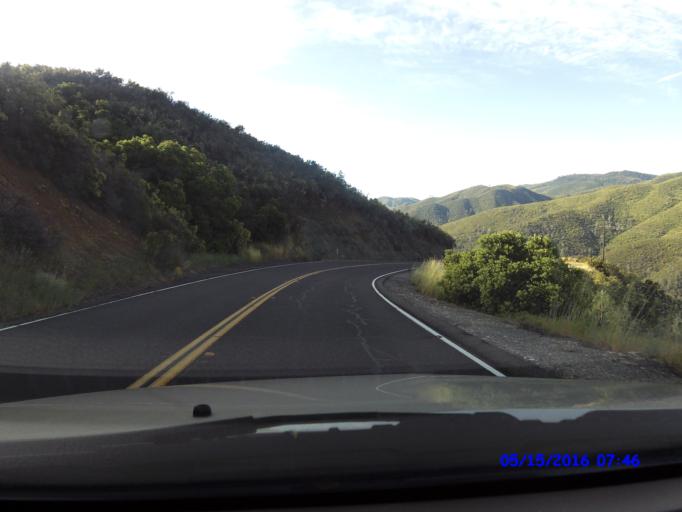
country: US
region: California
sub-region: Mariposa County
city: Mariposa
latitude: 37.6299
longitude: -120.1520
